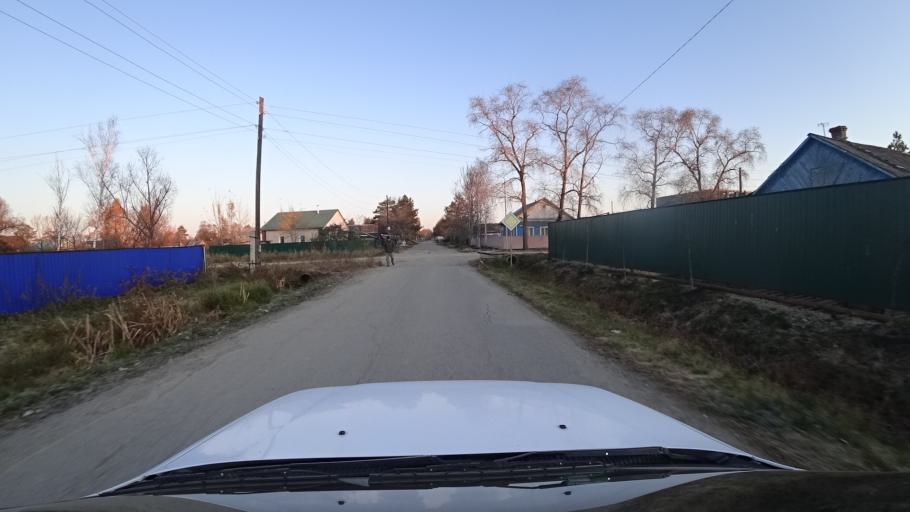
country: RU
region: Primorskiy
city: Dal'nerechensk
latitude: 45.9235
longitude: 133.7366
